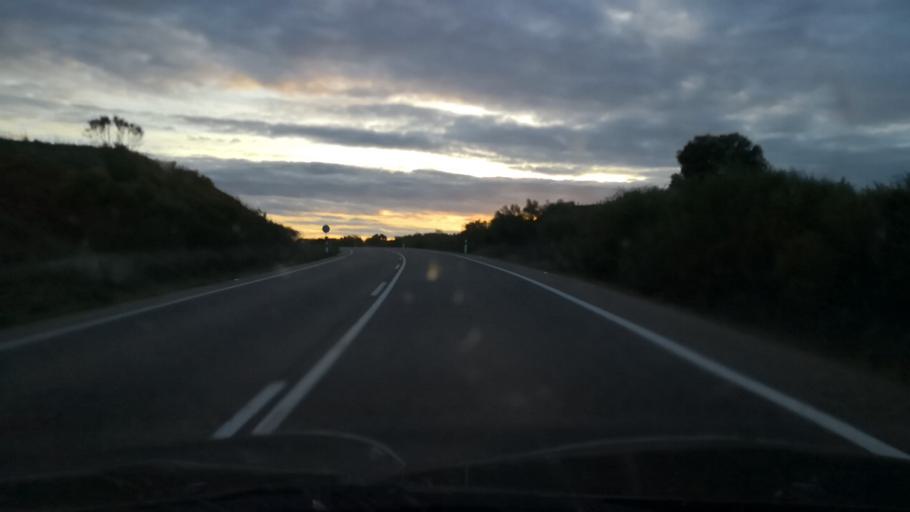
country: ES
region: Extremadura
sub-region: Provincia de Badajoz
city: Villar del Rey
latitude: 39.0578
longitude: -6.7865
